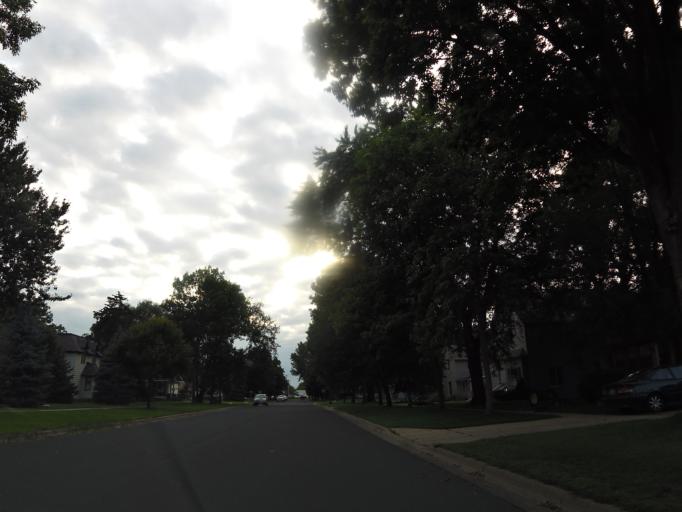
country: US
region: Minnesota
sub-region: Dakota County
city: Farmington
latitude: 44.6416
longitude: -93.1420
